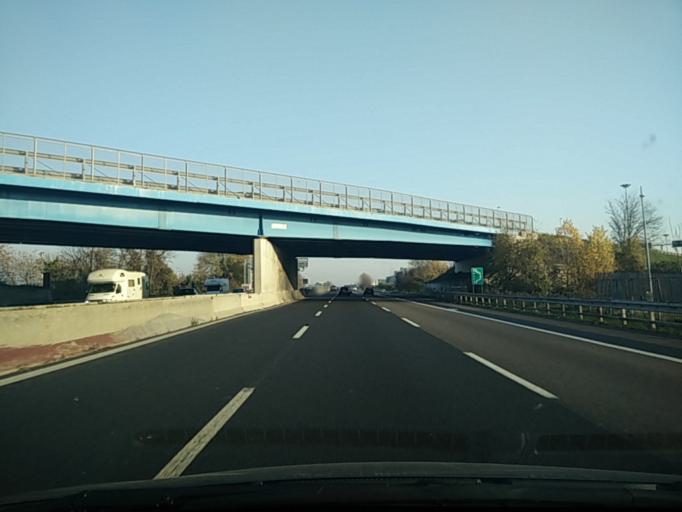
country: IT
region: Lombardy
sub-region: Provincia di Bergamo
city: Orio al Serio
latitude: 45.6665
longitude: 9.6886
